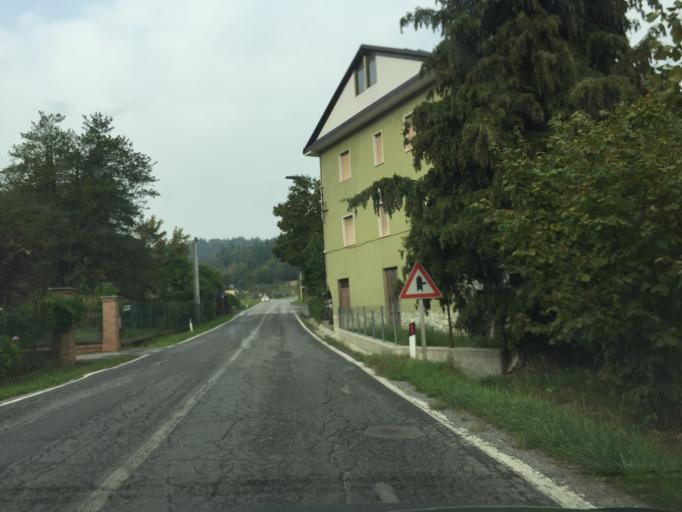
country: IT
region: Piedmont
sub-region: Provincia di Cuneo
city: Roccaforte Mondovi
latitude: 44.3106
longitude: 7.7199
